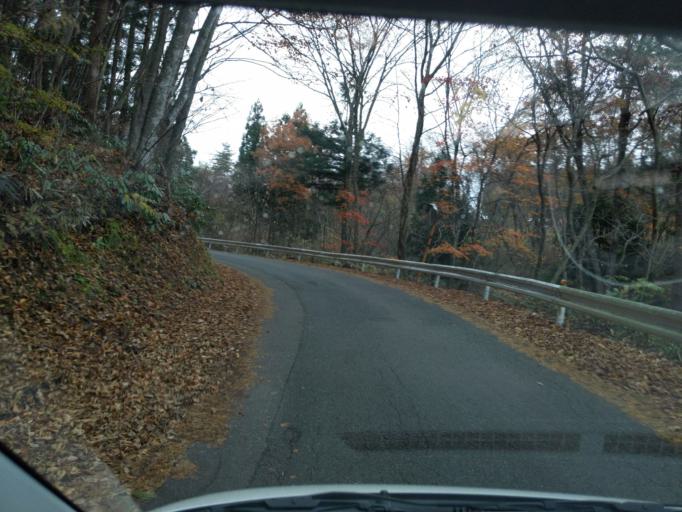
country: JP
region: Iwate
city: Ichinoseki
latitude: 38.9821
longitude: 141.0029
